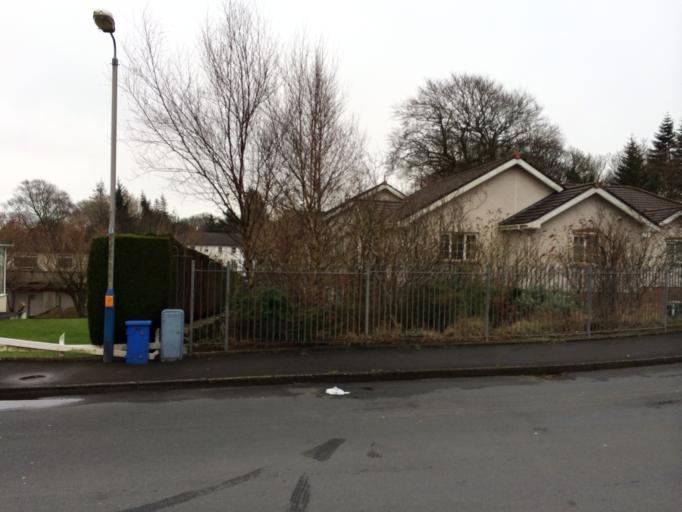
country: IM
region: Douglas
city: Douglas
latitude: 54.1561
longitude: -4.5108
